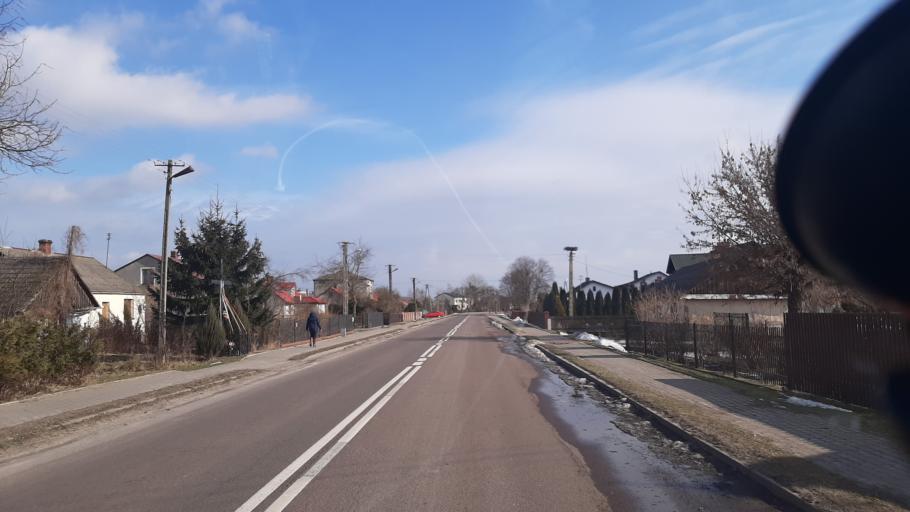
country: PL
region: Lublin Voivodeship
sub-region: Powiat wlodawski
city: Hansk
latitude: 51.4804
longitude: 23.2934
